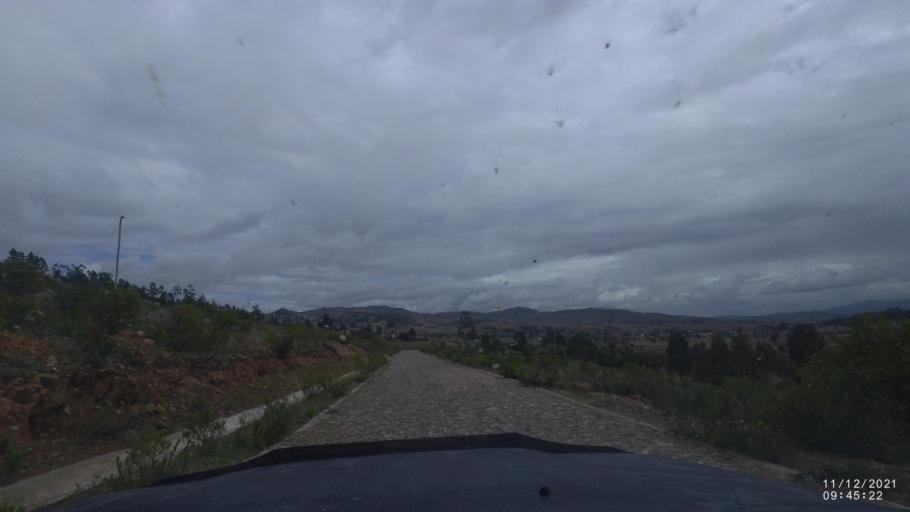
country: BO
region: Cochabamba
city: Tarata
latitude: -17.7910
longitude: -65.9729
